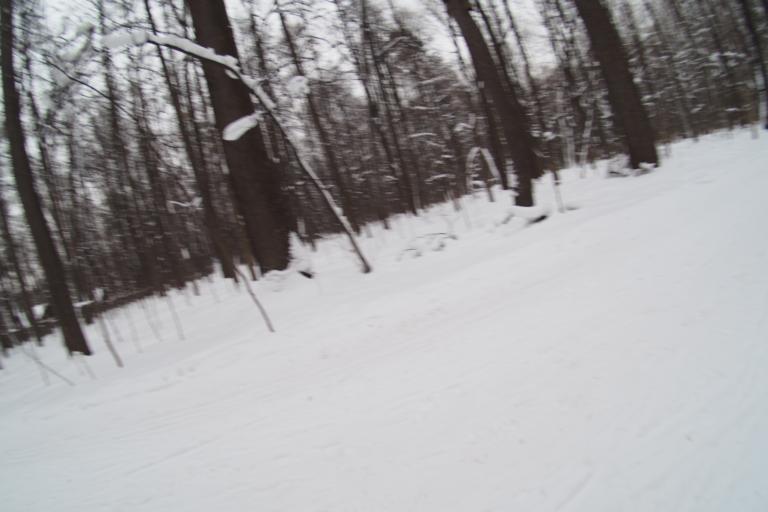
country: RU
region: Moskovskaya
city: Izmaylovo
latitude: 55.7739
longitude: 37.7868
